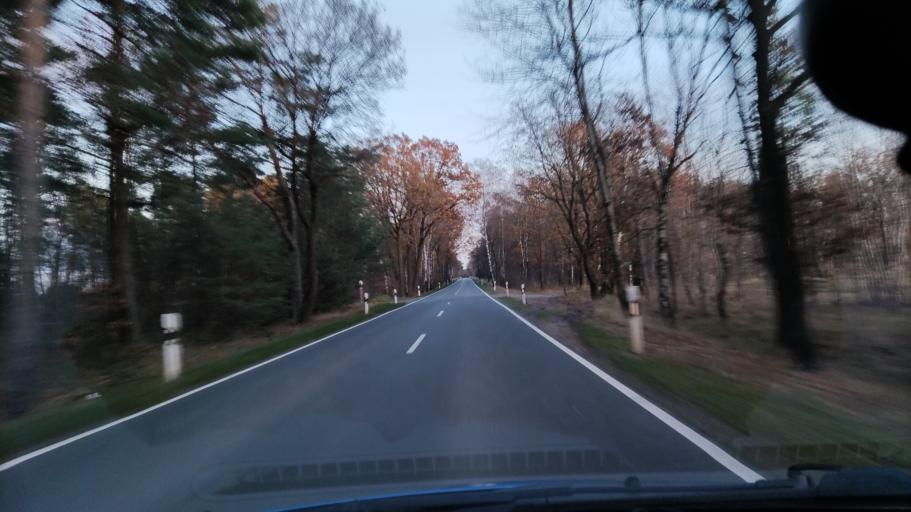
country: DE
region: Lower Saxony
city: Schneverdingen
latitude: 53.1255
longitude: 9.8234
